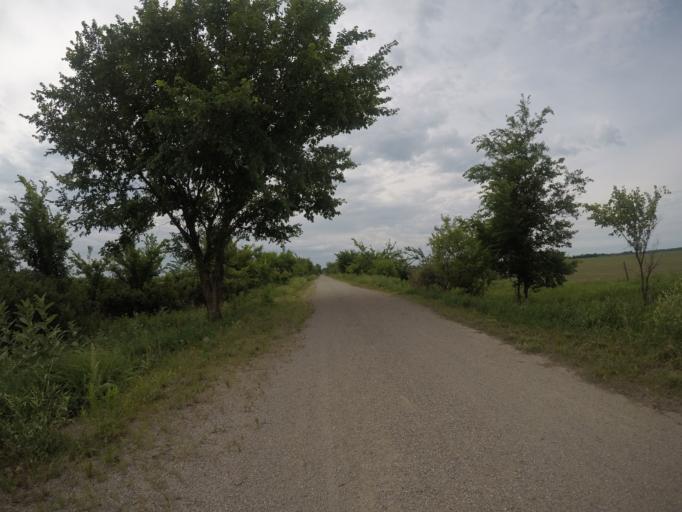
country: US
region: Kansas
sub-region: Franklin County
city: Ottawa
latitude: 38.4589
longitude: -95.2696
